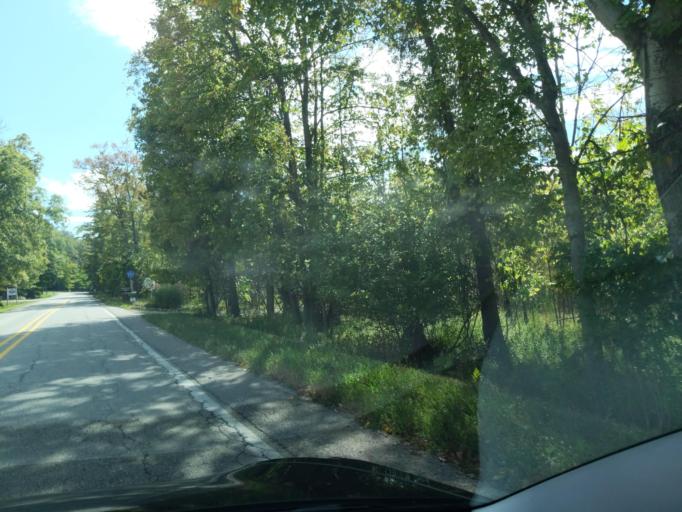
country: US
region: Michigan
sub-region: Antrim County
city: Bellaire
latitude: 45.0664
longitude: -85.3174
